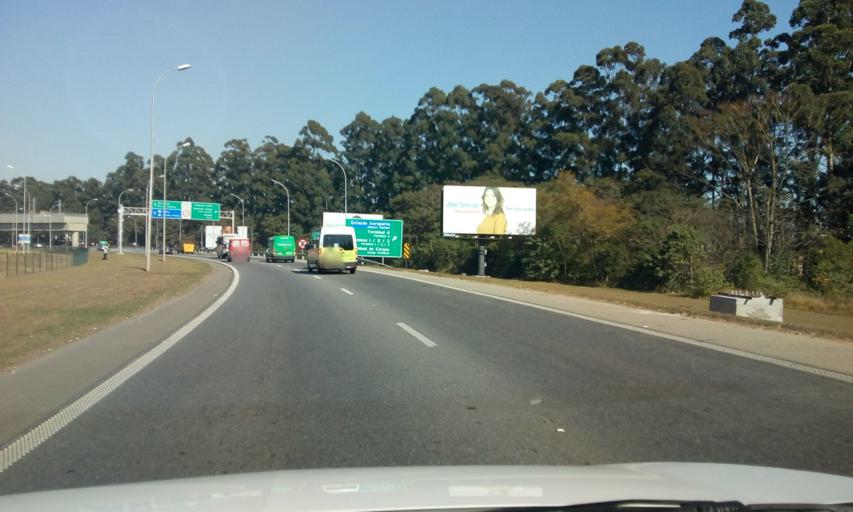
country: BR
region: Sao Paulo
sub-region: Guarulhos
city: Guarulhos
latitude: -23.4243
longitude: -46.4908
